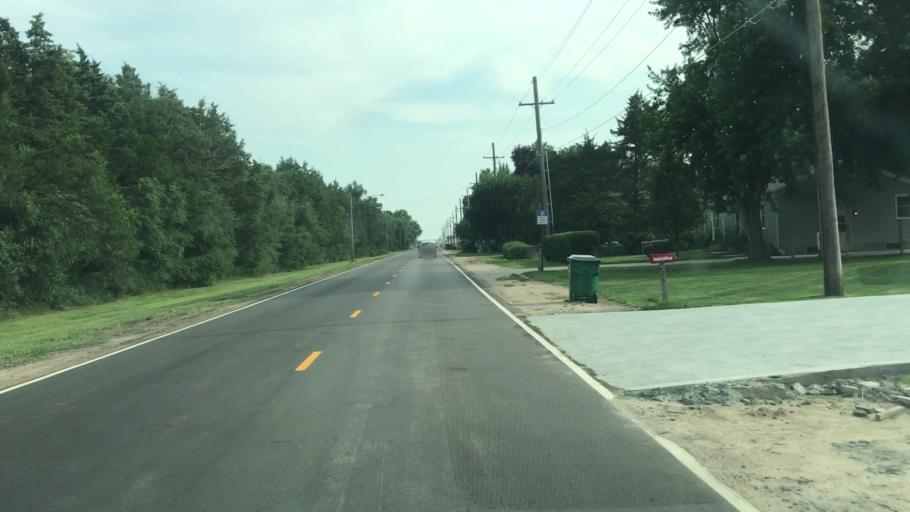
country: US
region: Nebraska
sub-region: Hall County
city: Grand Island
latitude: 40.9509
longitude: -98.3788
